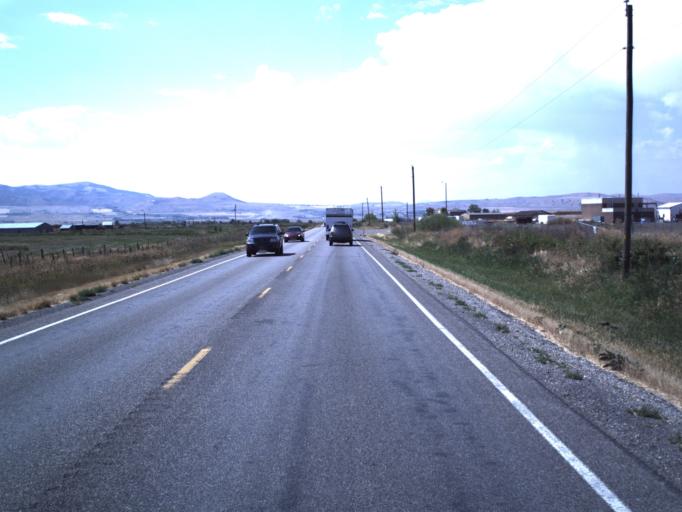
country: US
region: Utah
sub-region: Cache County
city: Benson
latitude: 41.7383
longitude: -111.8978
